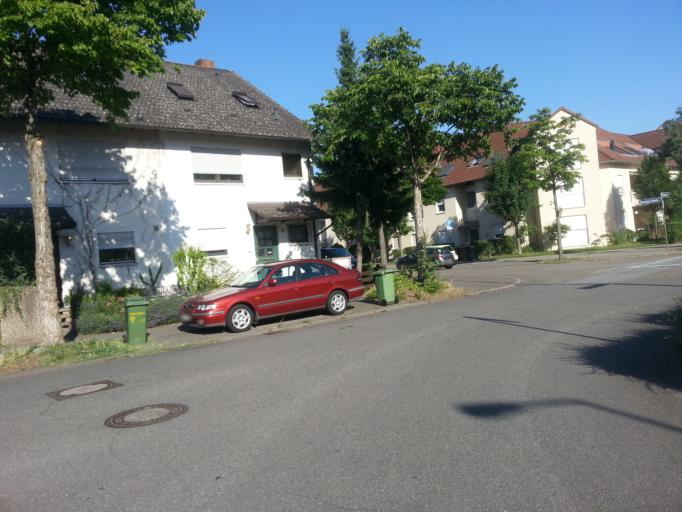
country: DE
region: Baden-Wuerttemberg
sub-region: Karlsruhe Region
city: Ilvesheim
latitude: 49.4664
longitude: 8.5512
